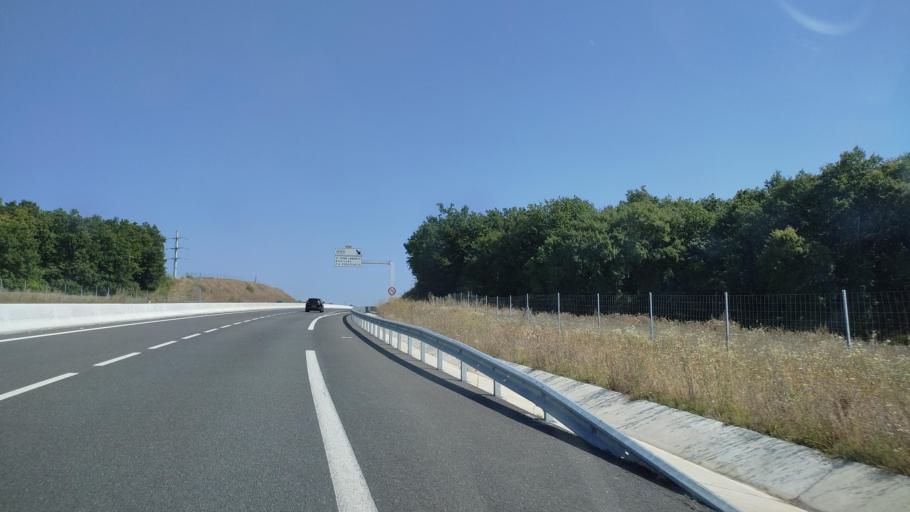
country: FR
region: Poitou-Charentes
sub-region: Departement de la Charente
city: Balzac
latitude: 45.6934
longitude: 0.0964
